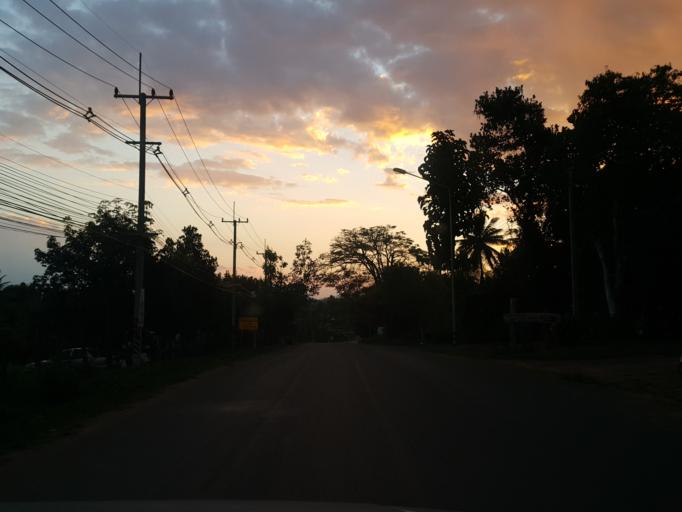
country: TH
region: Mae Hong Son
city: Khun Yuam
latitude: 18.8375
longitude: 97.9459
